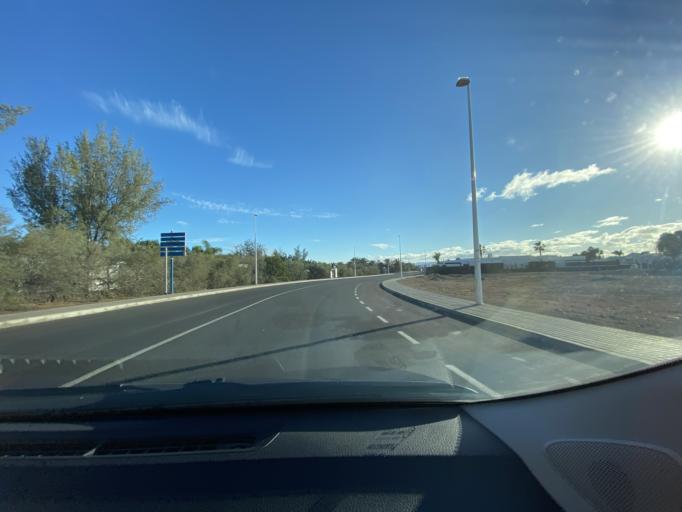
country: ES
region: Canary Islands
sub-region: Provincia de Las Palmas
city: Playa Blanca
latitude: 28.8655
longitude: -13.8412
